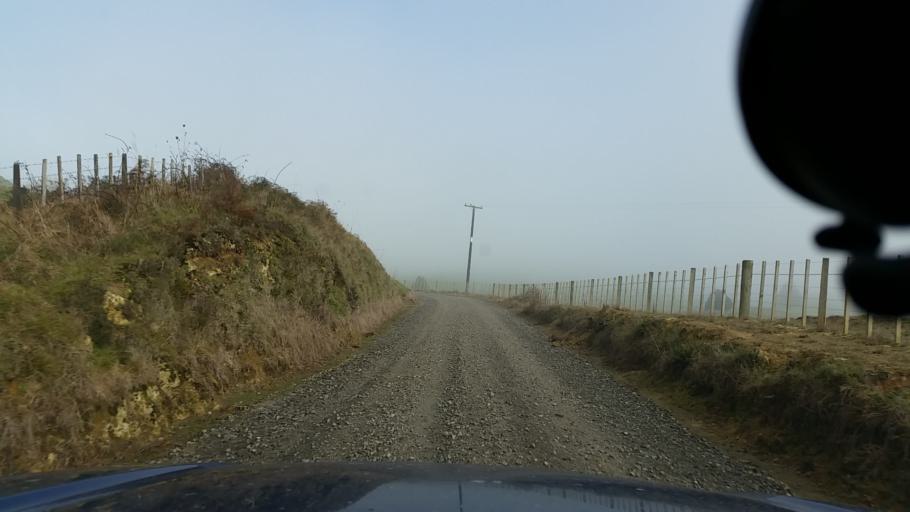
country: NZ
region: Taranaki
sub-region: New Plymouth District
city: Waitara
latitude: -38.9955
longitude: 174.7736
